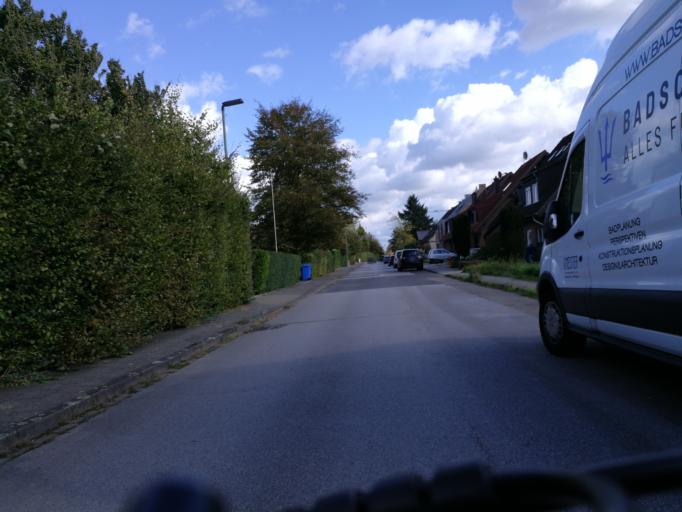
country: DE
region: North Rhine-Westphalia
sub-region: Regierungsbezirk Dusseldorf
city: Neuss
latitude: 51.1429
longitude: 6.7193
